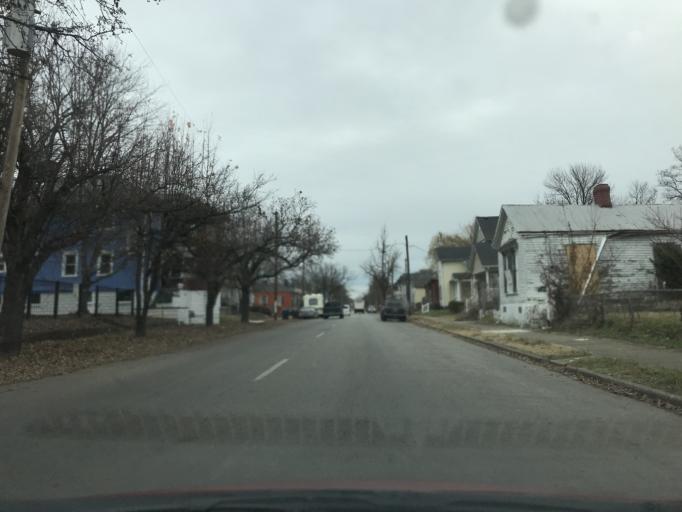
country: US
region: Kentucky
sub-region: Jefferson County
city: Louisville
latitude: 38.2522
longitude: -85.7860
